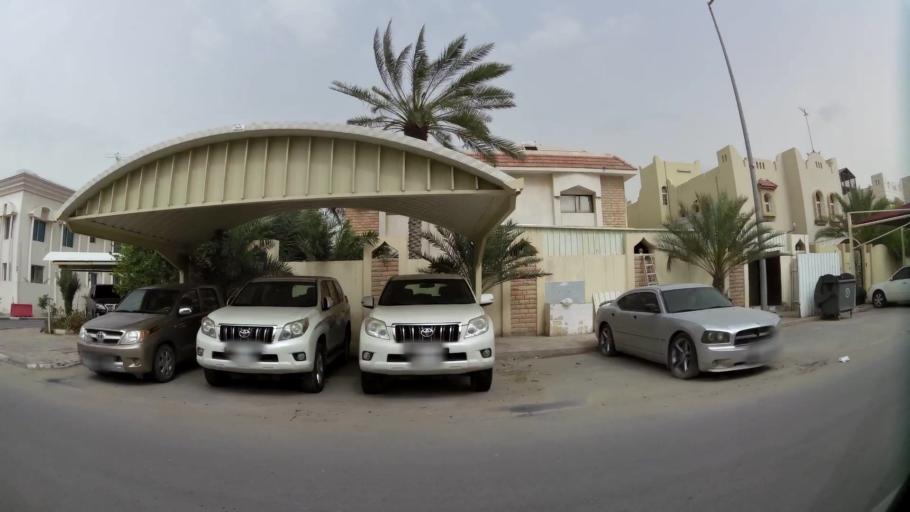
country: QA
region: Baladiyat ad Dawhah
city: Doha
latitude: 25.2453
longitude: 51.5364
